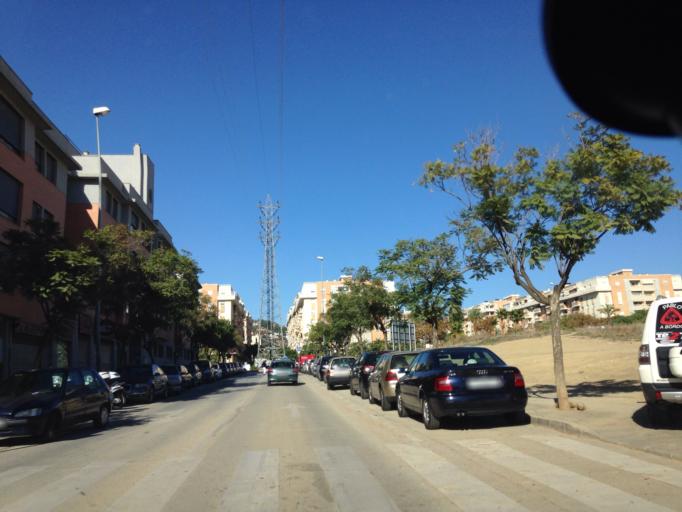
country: ES
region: Andalusia
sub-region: Provincia de Malaga
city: Malaga
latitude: 36.7232
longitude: -4.4746
